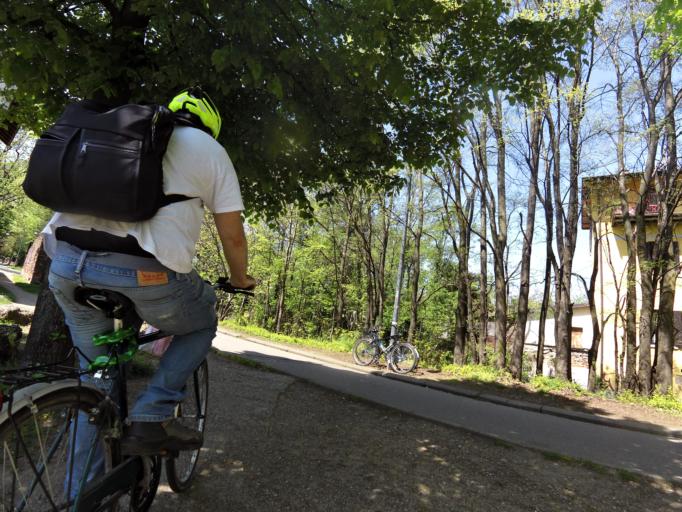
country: IT
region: Lombardy
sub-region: Citta metropolitana di Milano
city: Sesto San Giovanni
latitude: 45.5036
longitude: 9.2294
